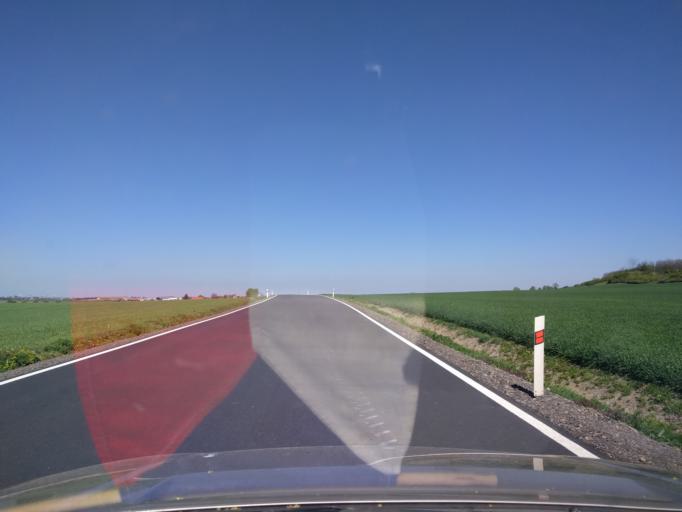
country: CZ
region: Central Bohemia
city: Prerov nad Labem
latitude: 50.1239
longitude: 14.8530
